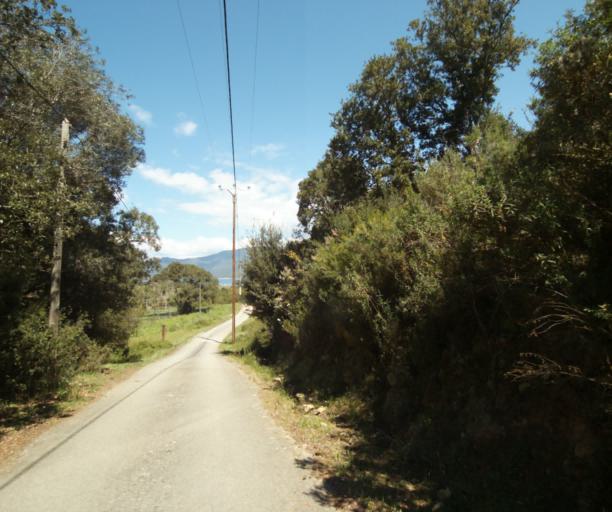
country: FR
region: Corsica
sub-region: Departement de la Corse-du-Sud
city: Propriano
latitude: 41.6404
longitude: 8.8688
